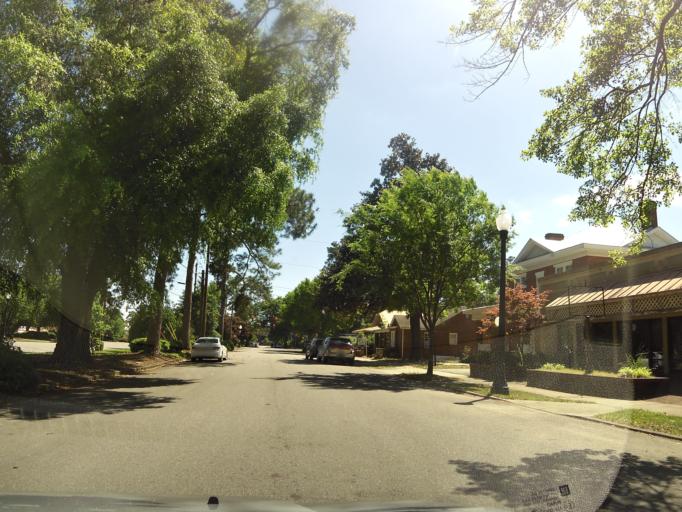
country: US
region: South Carolina
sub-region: Aiken County
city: Aiken
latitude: 33.5631
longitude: -81.7235
